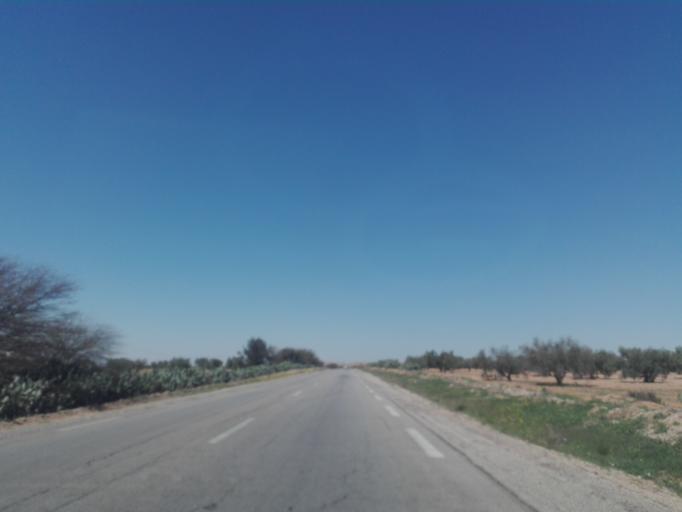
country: TN
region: Safaqis
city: Bi'r `Ali Bin Khalifah
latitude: 34.7571
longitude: 10.2662
